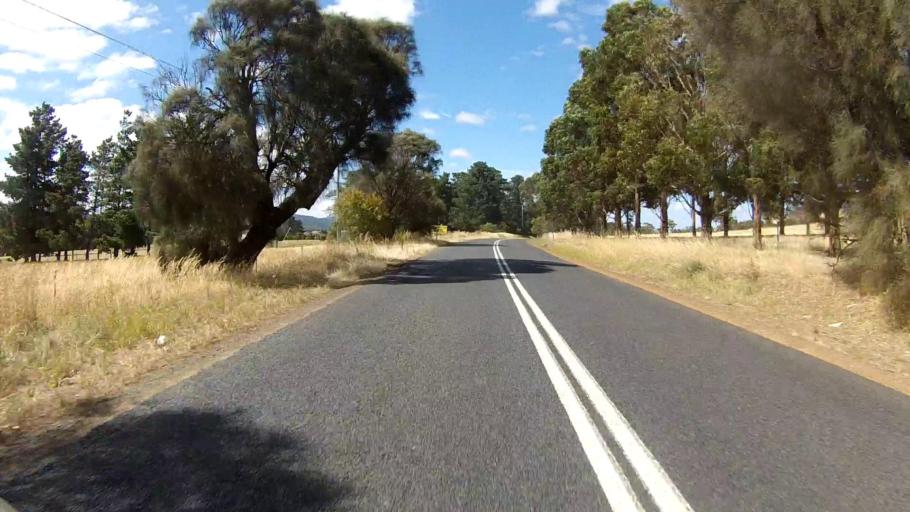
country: AU
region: Tasmania
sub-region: Sorell
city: Sorell
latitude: -42.6120
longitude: 147.4269
